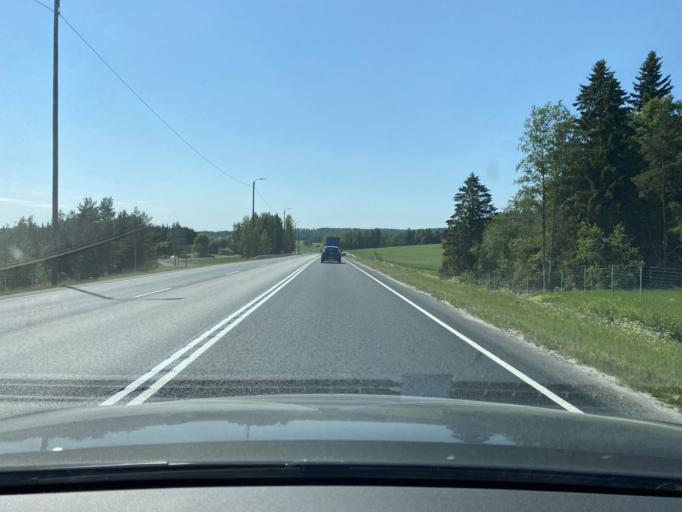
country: FI
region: Pirkanmaa
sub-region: Lounais-Pirkanmaa
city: Mouhijaervi
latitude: 61.3676
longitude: 23.1189
